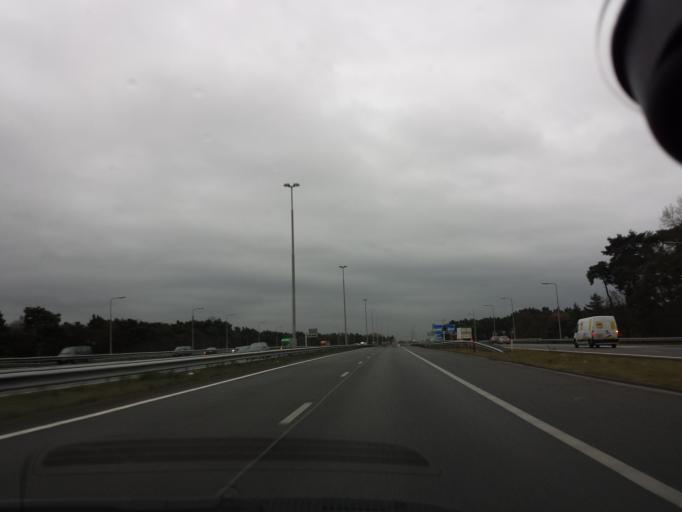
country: NL
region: Limburg
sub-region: Gemeente Venlo
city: Venlo
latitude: 51.3952
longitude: 6.1281
